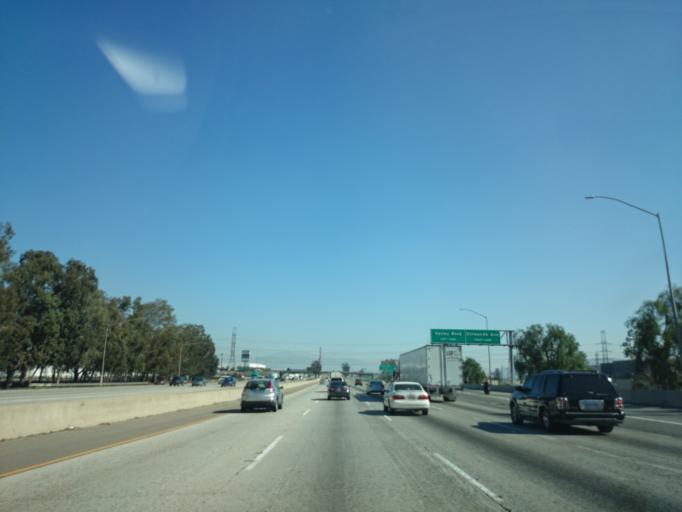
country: US
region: California
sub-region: Riverside County
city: Glen Avon
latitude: 34.0672
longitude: -117.5305
